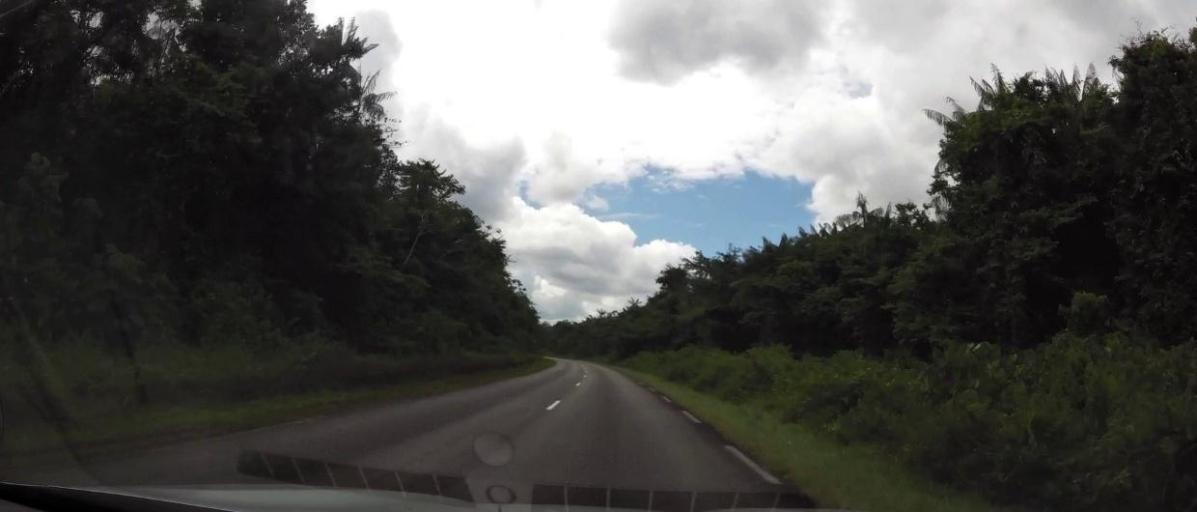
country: GF
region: Guyane
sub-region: Guyane
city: Sinnamary
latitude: 5.3676
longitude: -52.9620
